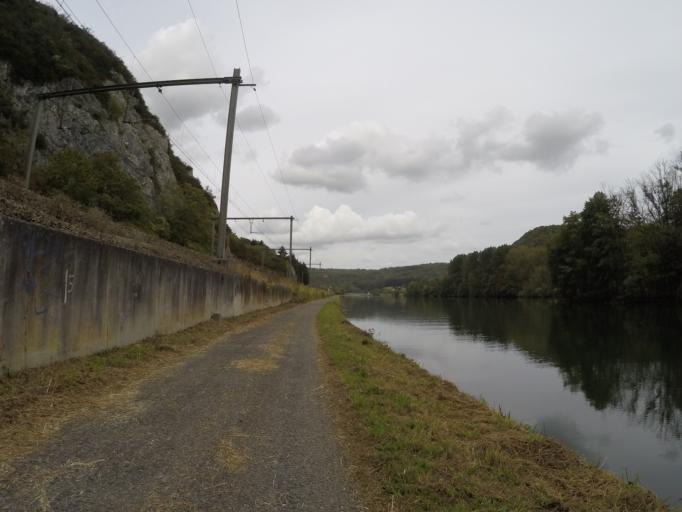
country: BE
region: Wallonia
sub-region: Province de Namur
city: Anhee
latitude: 50.2889
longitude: 4.8914
